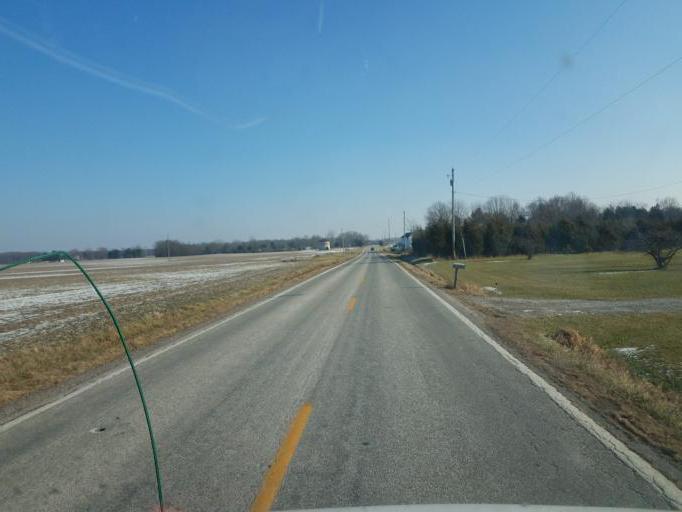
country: US
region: Ohio
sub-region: Morrow County
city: Cardington
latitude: 40.5240
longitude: -82.9593
